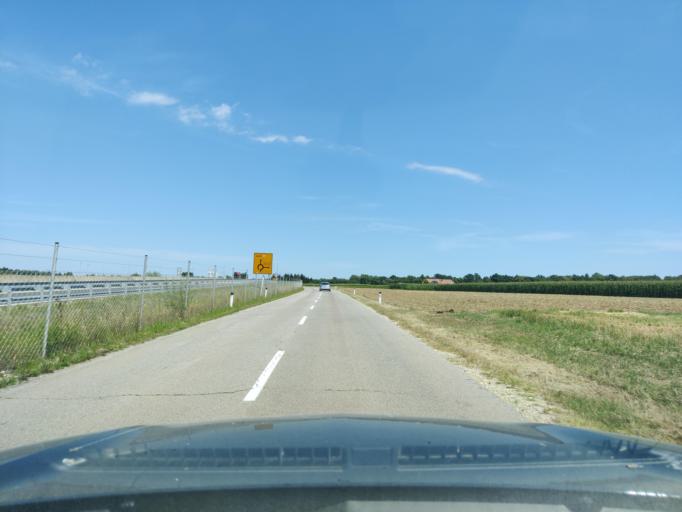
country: SI
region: Lendava-Lendva
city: Lendava
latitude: 46.5907
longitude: 16.4563
